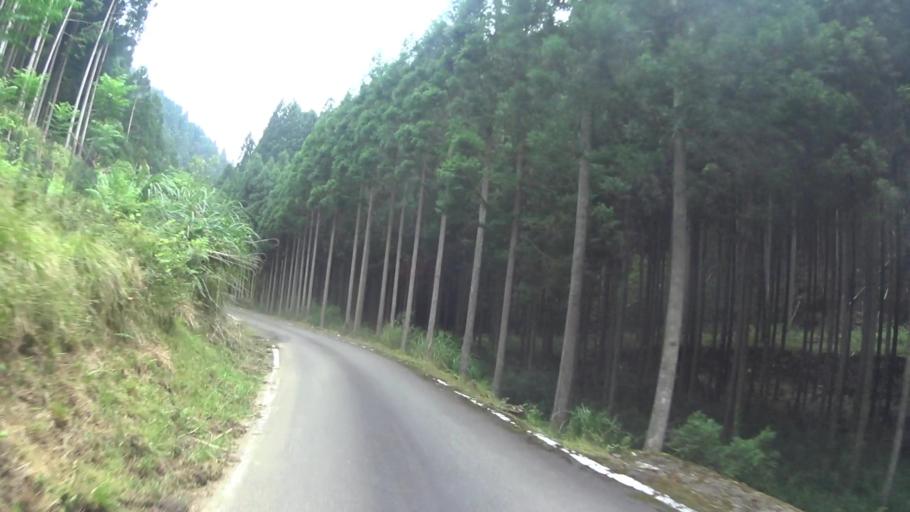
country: JP
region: Kyoto
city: Kameoka
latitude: 35.1651
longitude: 135.5762
